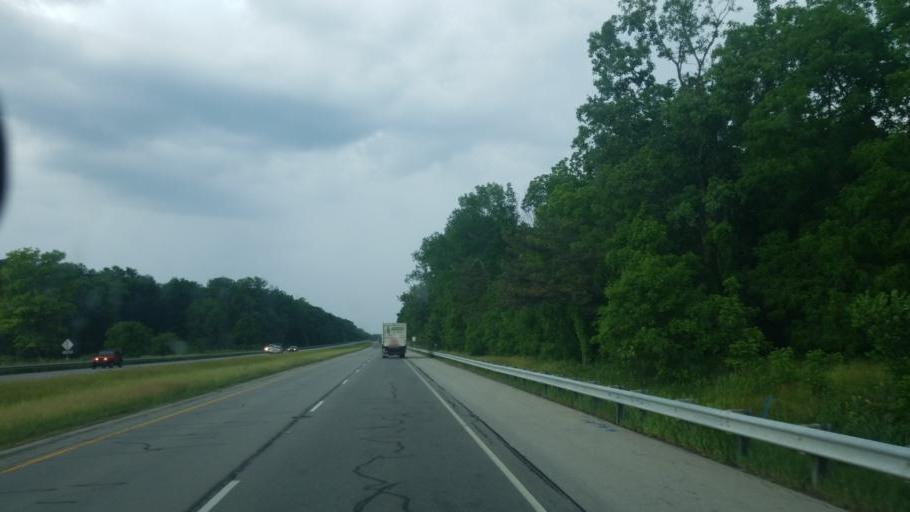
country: US
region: Indiana
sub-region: Whitley County
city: Churubusco
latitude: 41.1261
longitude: -85.3017
